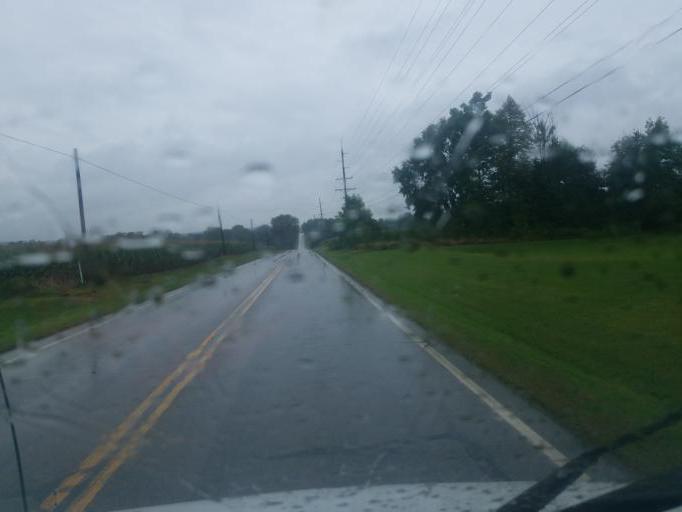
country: US
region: Ohio
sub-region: Medina County
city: Seville
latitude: 41.0252
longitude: -81.8454
